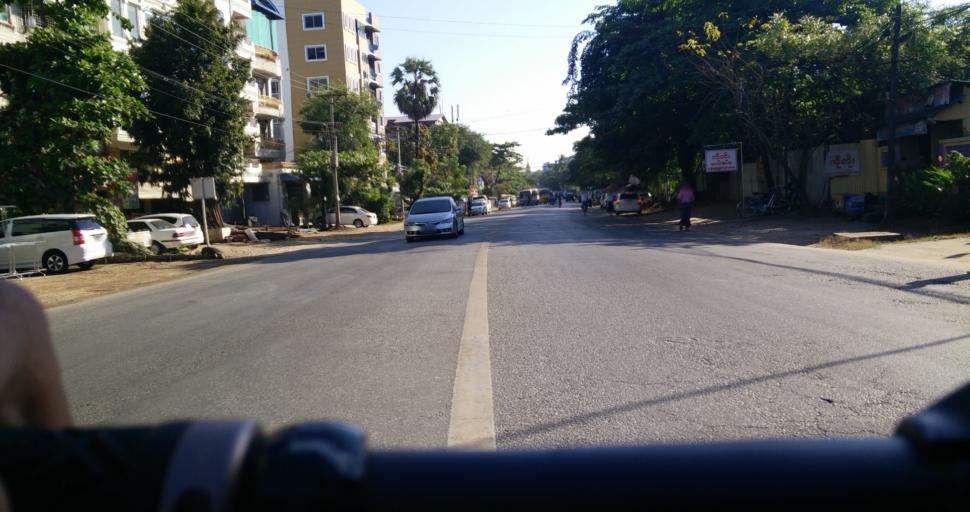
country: MM
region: Yangon
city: Yangon
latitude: 16.8380
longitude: 96.1888
